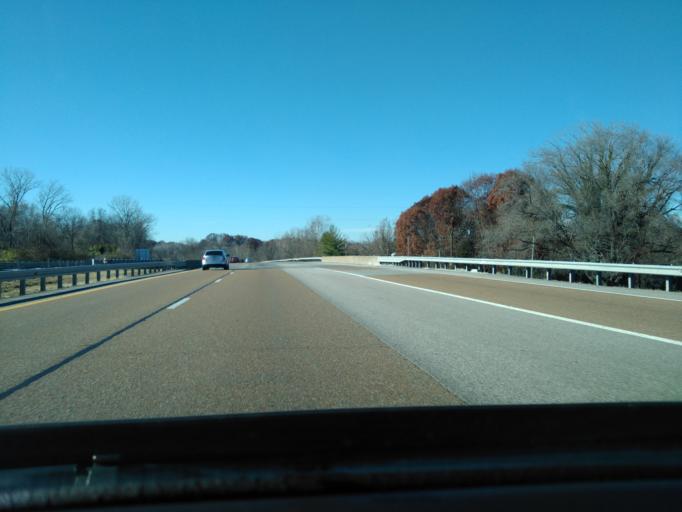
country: US
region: Illinois
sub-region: Madison County
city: Collinsville
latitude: 38.7027
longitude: -89.9840
